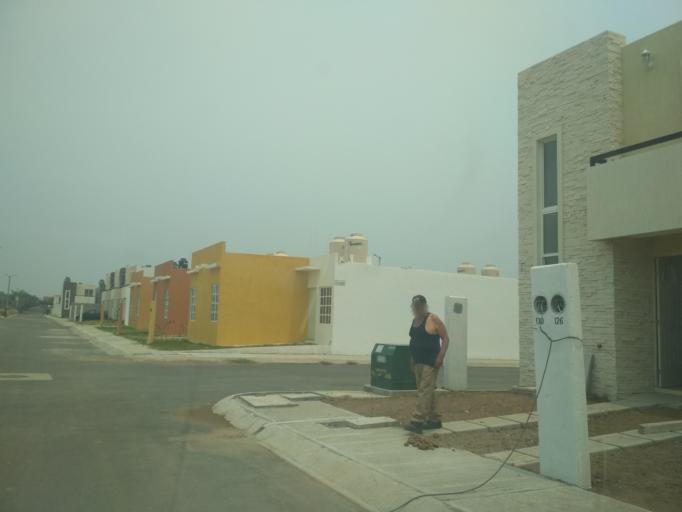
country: MX
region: Veracruz
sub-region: Veracruz
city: Las Amapolas
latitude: 19.1524
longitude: -96.2177
